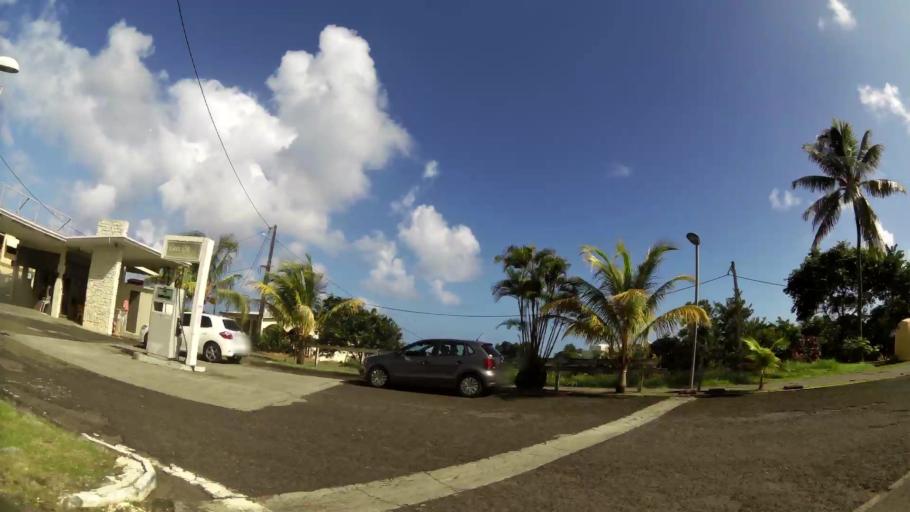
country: MQ
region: Martinique
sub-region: Martinique
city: Le Lorrain
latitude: 14.8322
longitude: -61.0480
